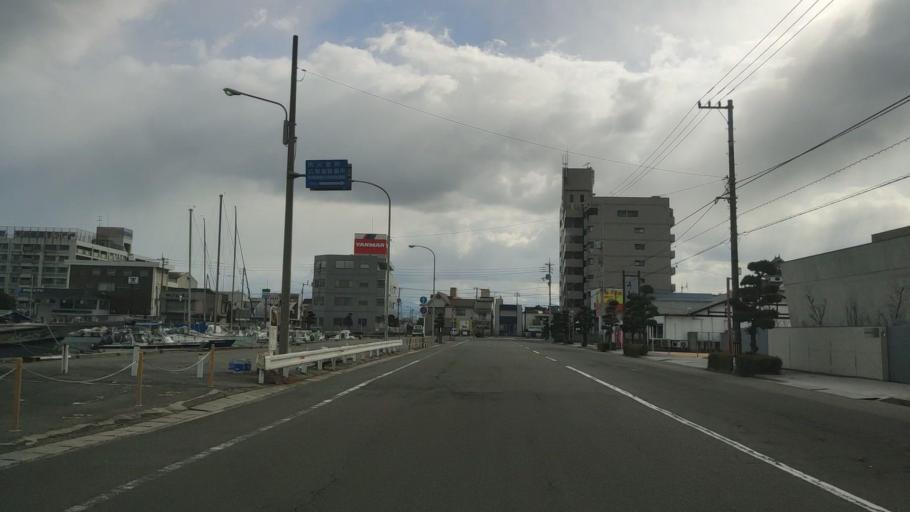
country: JP
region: Ehime
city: Saijo
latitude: 34.0667
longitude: 133.0060
